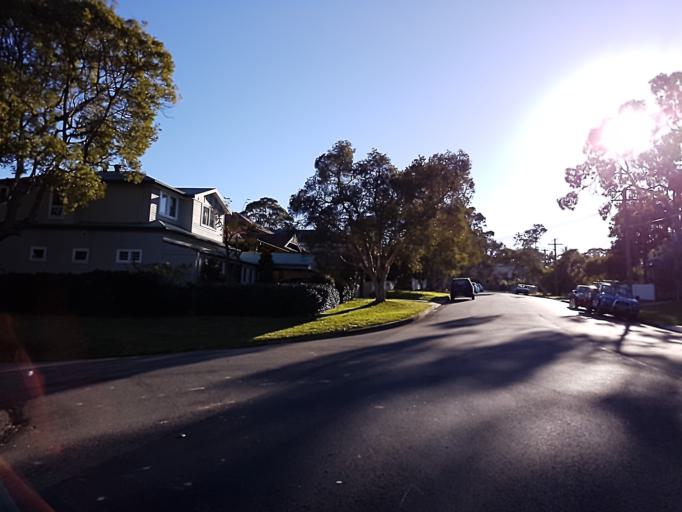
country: AU
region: New South Wales
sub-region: Manly Vale
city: Balgowlah
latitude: -33.7885
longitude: 151.2479
